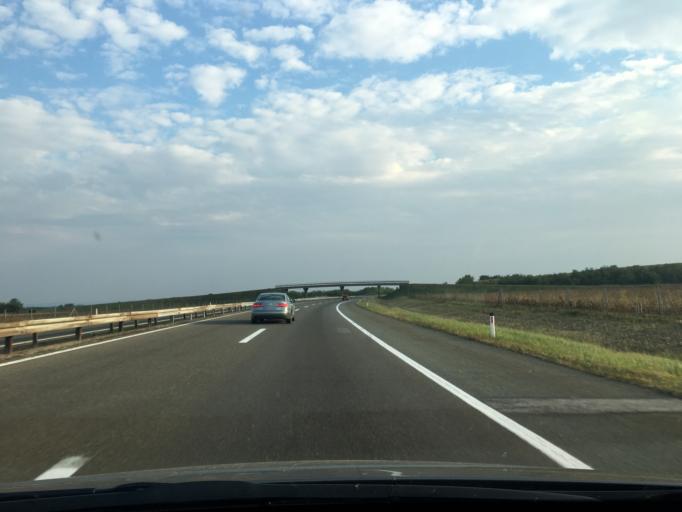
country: RS
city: Lugavcina
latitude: 44.5057
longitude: 21.0211
